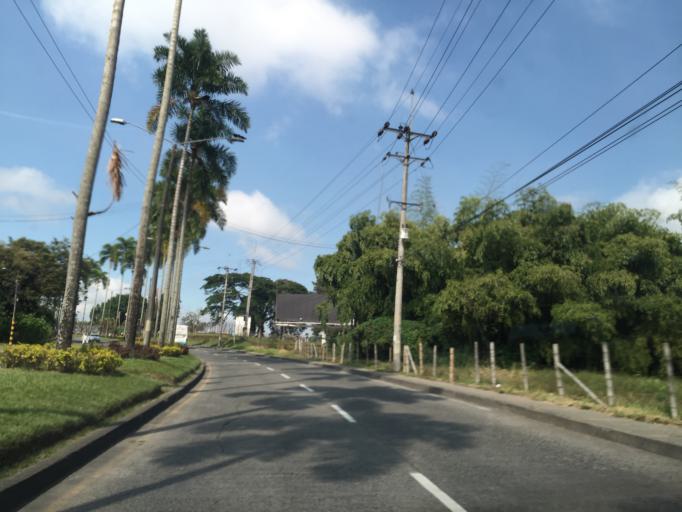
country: CO
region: Risaralda
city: Pereira
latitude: 4.8084
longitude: -75.7279
